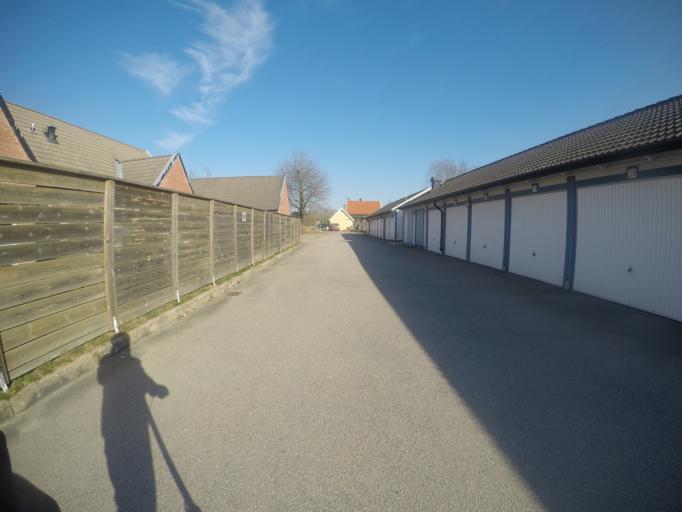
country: SE
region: Halland
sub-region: Laholms Kommun
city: Laholm
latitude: 56.5040
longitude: 13.0601
